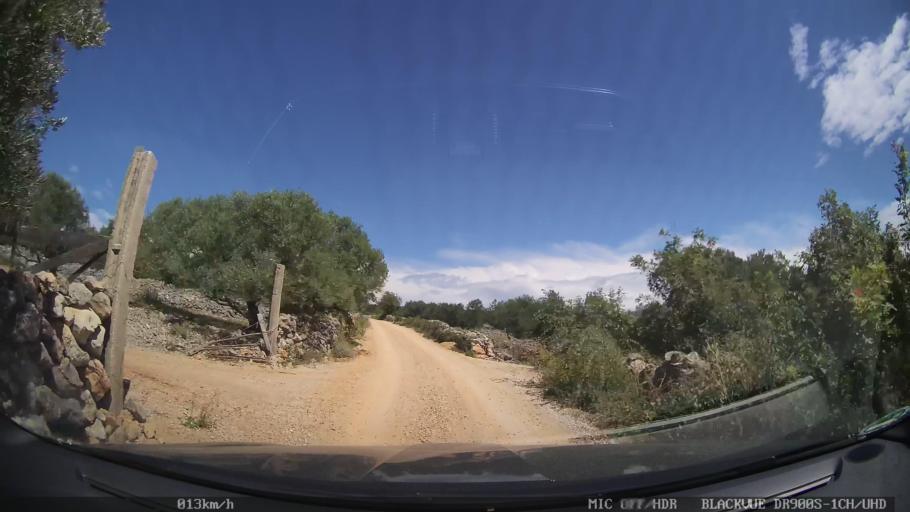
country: HR
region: Primorsko-Goranska
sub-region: Grad Krk
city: Krk
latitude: 45.0269
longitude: 14.5243
